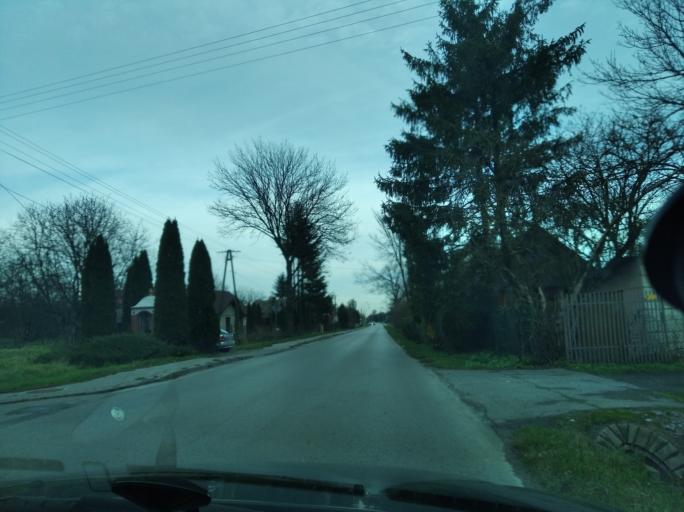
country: PL
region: Subcarpathian Voivodeship
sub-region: Powiat przeworski
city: Przeworsk
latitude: 50.0526
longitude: 22.4725
